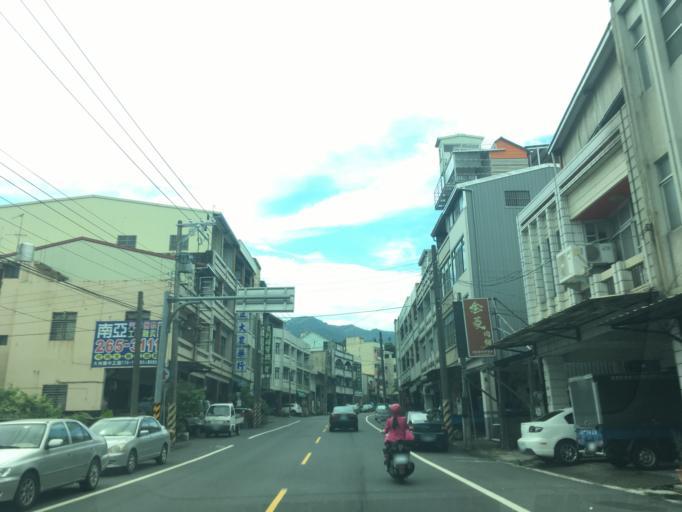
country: TW
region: Taiwan
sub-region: Yunlin
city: Douliu
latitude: 23.5833
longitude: 120.5603
